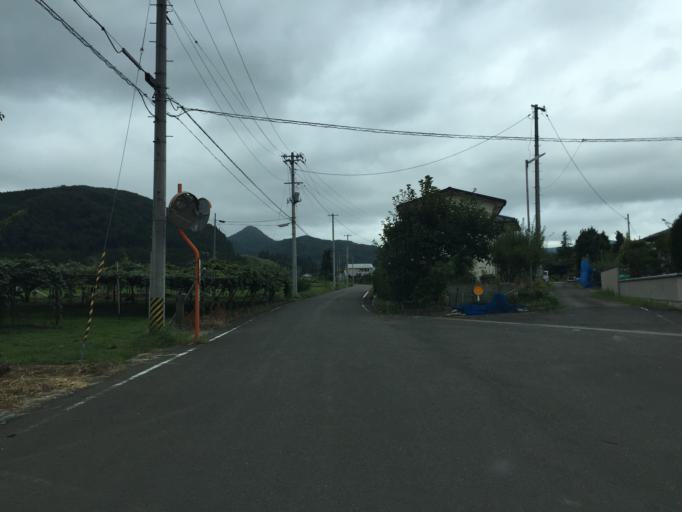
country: JP
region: Fukushima
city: Fukushima-shi
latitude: 37.7795
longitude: 140.3831
